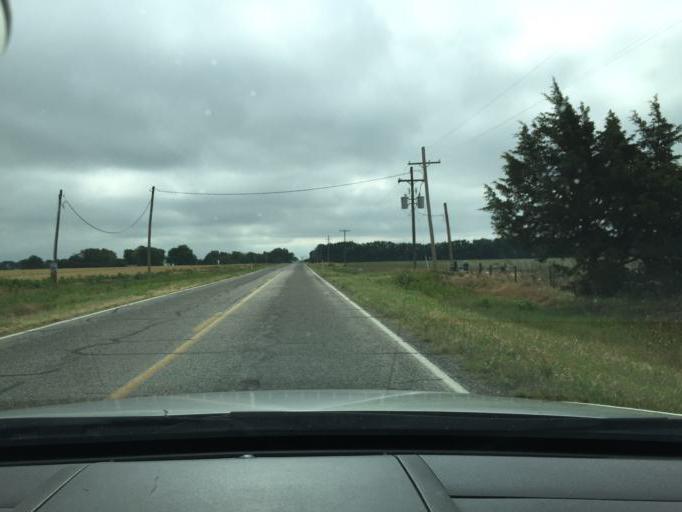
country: US
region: Kansas
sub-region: Reno County
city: South Hutchinson
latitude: 37.9700
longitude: -98.0280
